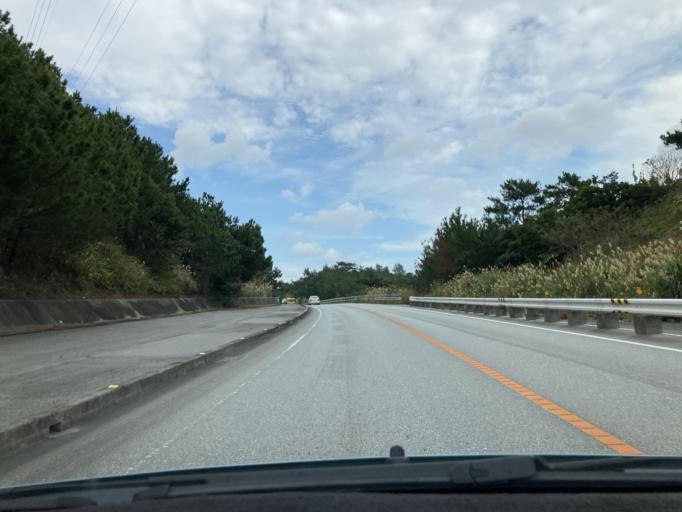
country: JP
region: Okinawa
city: Ishikawa
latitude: 26.4833
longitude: 127.8524
